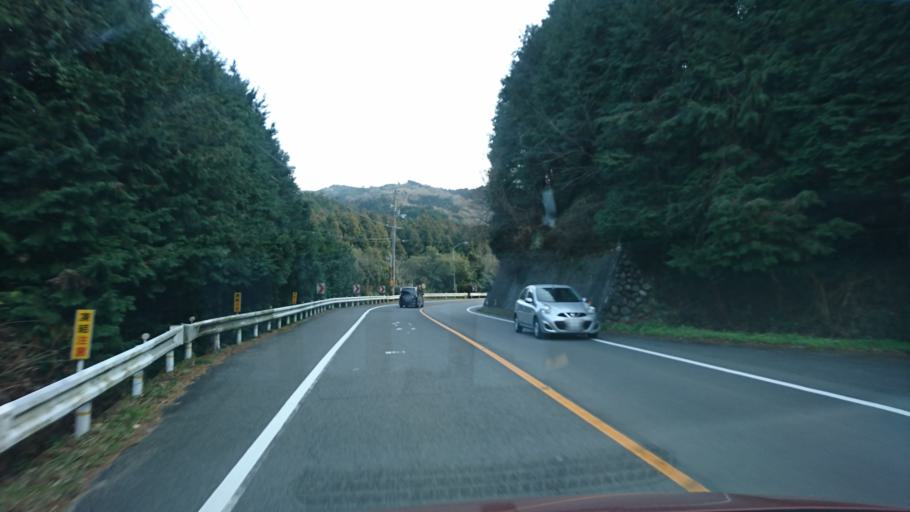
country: JP
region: Ehime
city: Hojo
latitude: 33.9848
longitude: 132.9084
